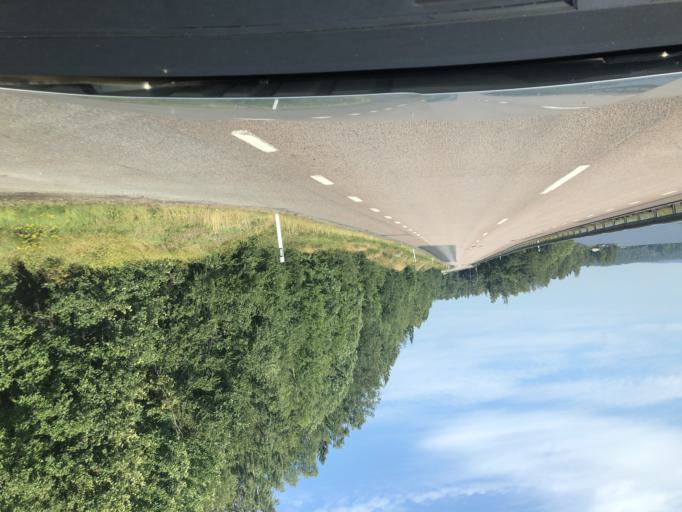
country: SE
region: Vaesternorrland
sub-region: Kramfors Kommun
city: Kramfors
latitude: 62.7967
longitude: 17.8822
